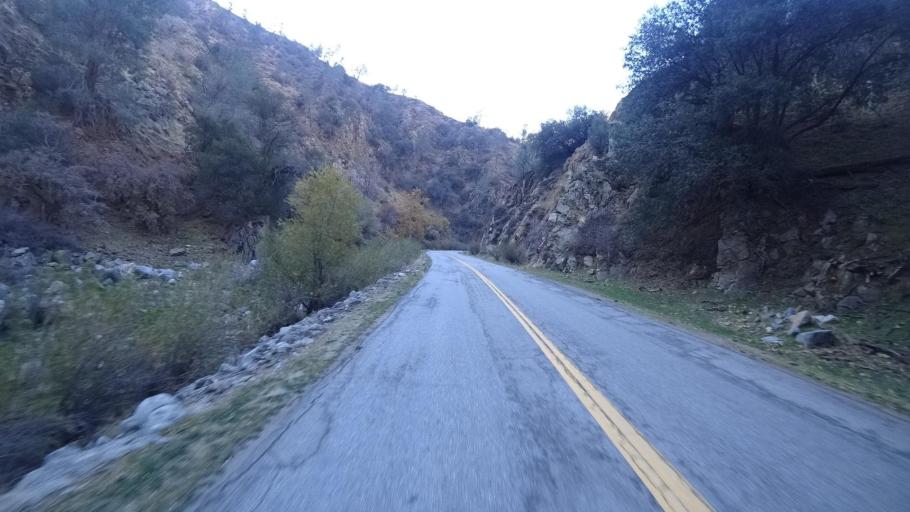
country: US
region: California
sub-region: Kern County
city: Golden Hills
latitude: 35.3143
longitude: -118.5283
